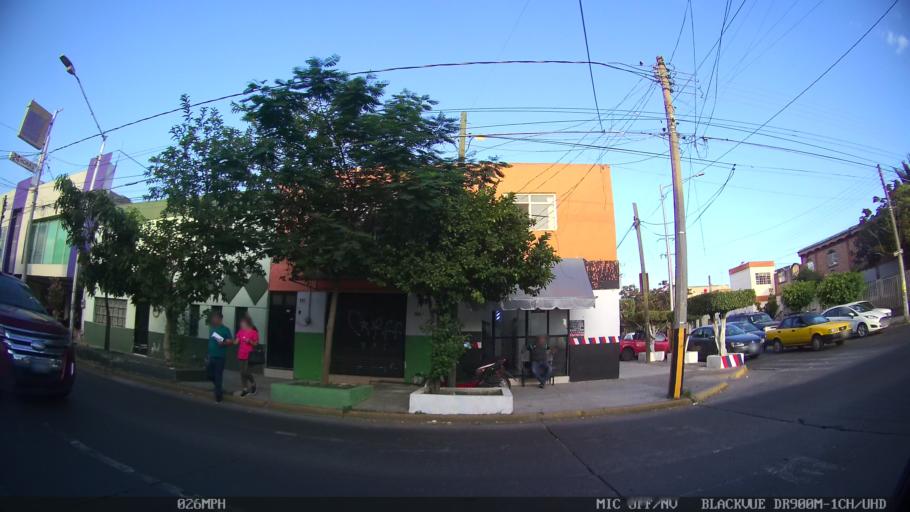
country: MX
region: Jalisco
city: Tlaquepaque
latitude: 20.6807
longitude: -103.3109
